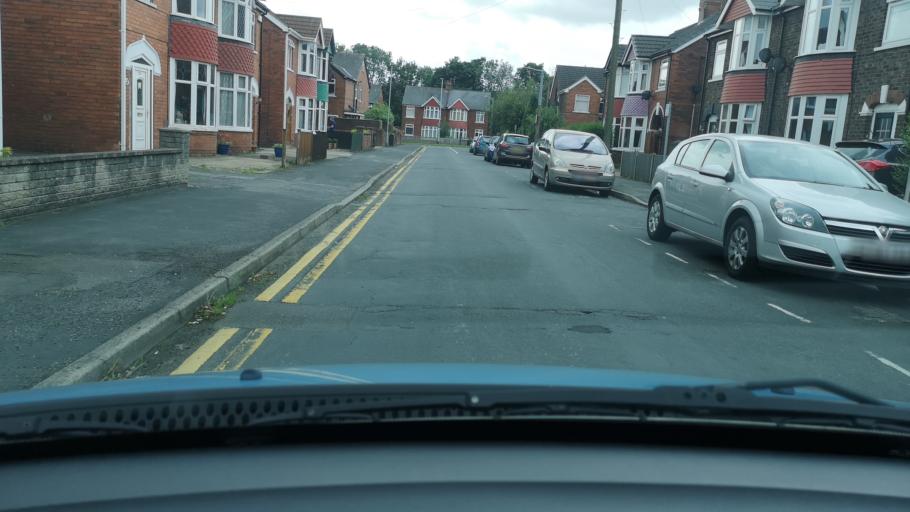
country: GB
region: England
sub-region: North Lincolnshire
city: Scunthorpe
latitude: 53.5869
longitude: -0.6644
